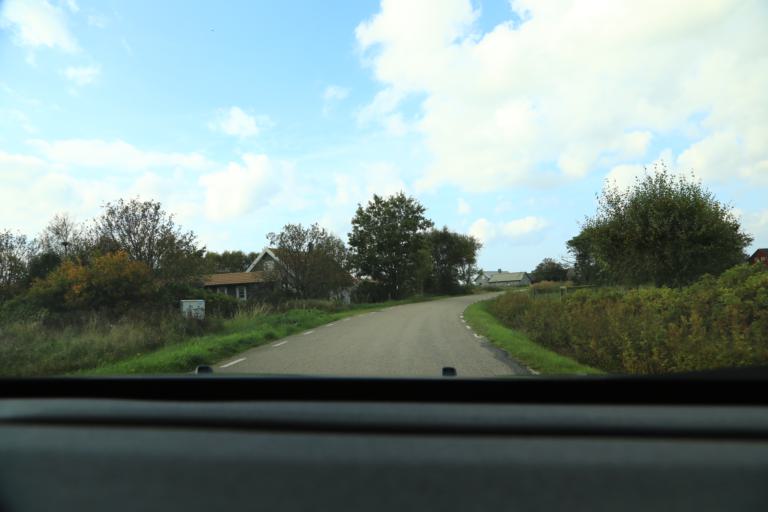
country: SE
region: Halland
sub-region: Varbergs Kommun
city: Traslovslage
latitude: 57.0274
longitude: 12.3174
